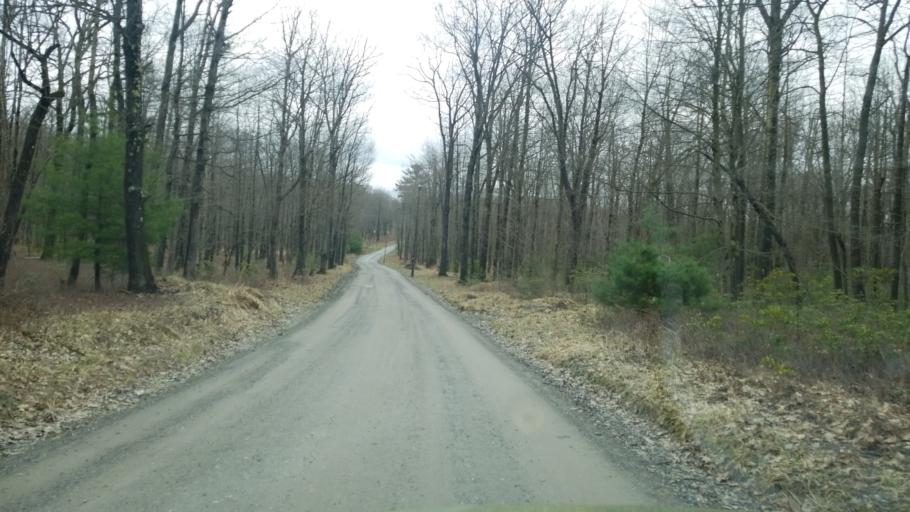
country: US
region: Pennsylvania
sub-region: Clearfield County
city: Shiloh
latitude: 41.1767
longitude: -78.3180
